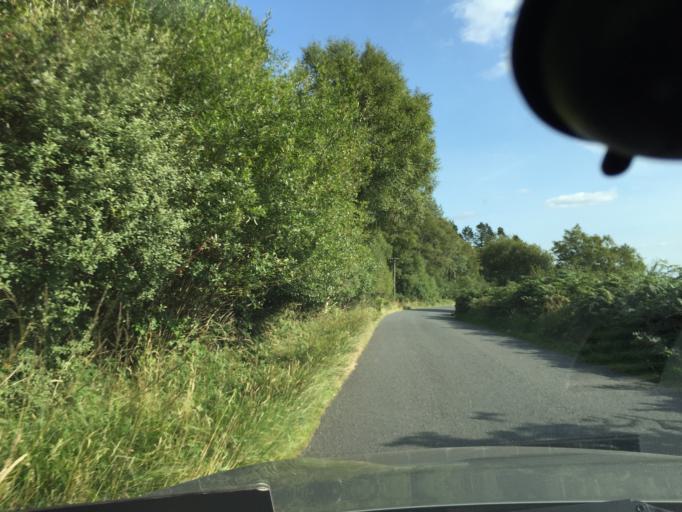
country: IE
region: Leinster
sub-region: Wicklow
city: Rathdrum
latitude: 53.0209
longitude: -6.3055
